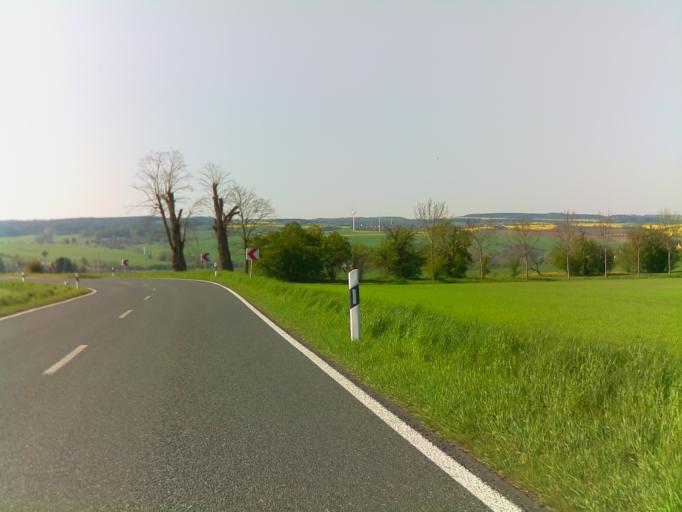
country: DE
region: Thuringia
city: Neustadt (Orla)
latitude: 50.7429
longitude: 11.7253
